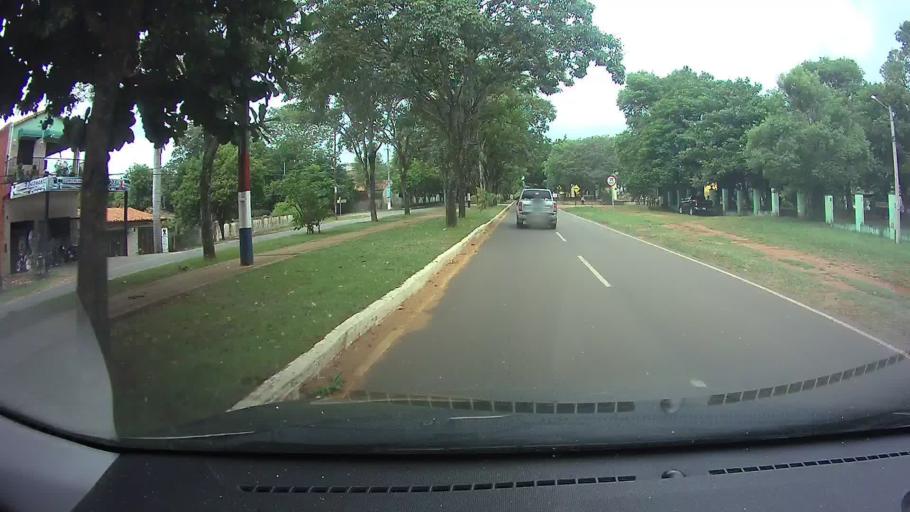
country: PY
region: Central
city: Nueva Italia
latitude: -25.6107
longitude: -57.4717
